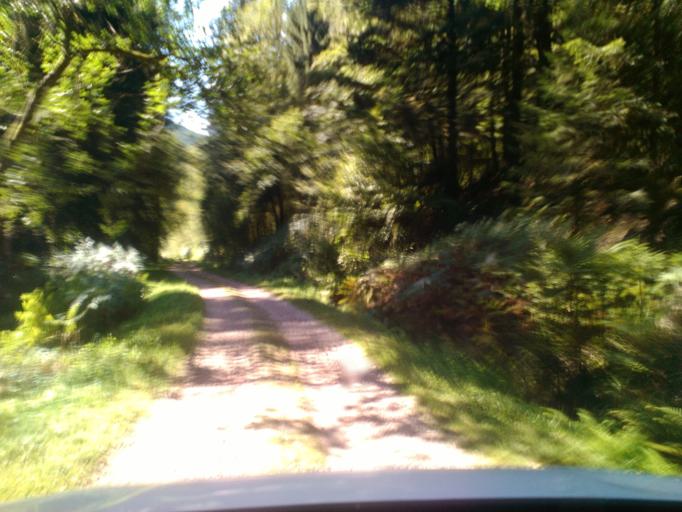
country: FR
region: Lorraine
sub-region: Departement des Vosges
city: Senones
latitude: 48.4255
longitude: 6.9517
